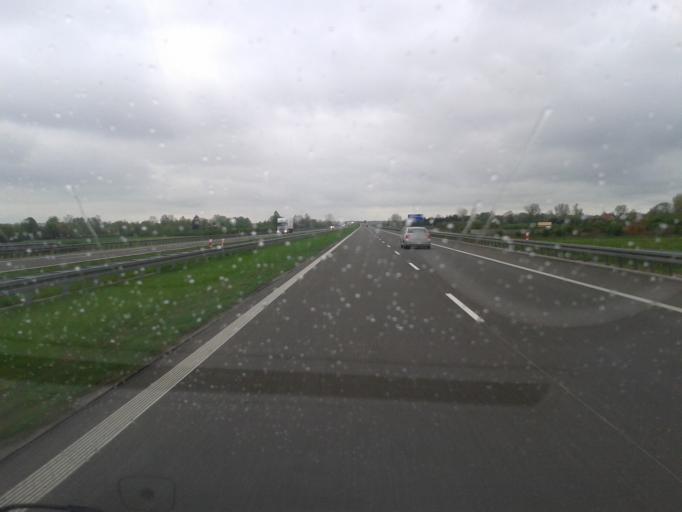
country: PL
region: Subcarpathian Voivodeship
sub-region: Powiat lancucki
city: Gluchow
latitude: 50.1024
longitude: 22.2714
